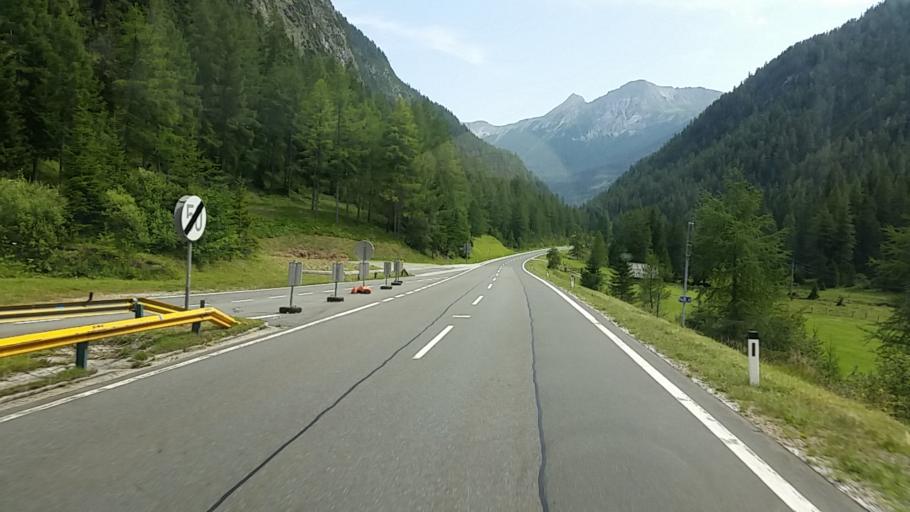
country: AT
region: Salzburg
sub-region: Politischer Bezirk Tamsweg
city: Tweng
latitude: 47.2208
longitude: 13.5818
